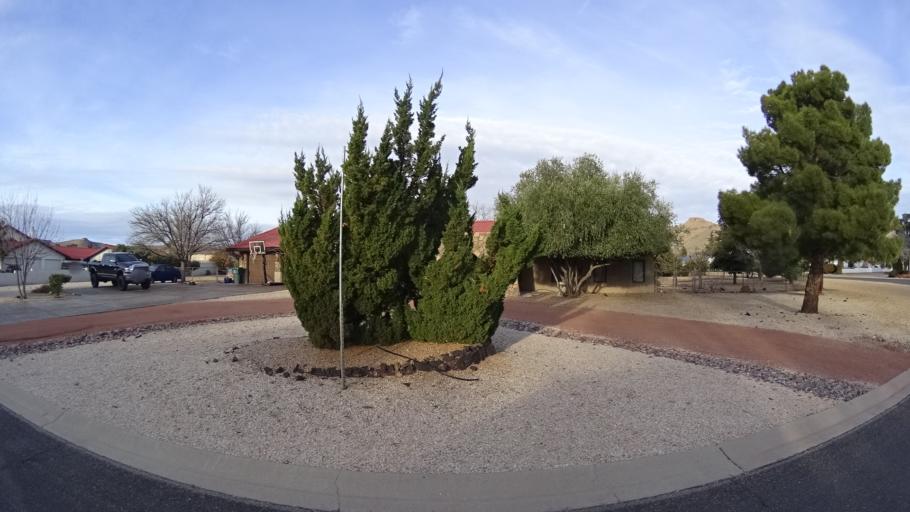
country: US
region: Arizona
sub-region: Mohave County
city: New Kingman-Butler
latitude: 35.2429
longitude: -114.0439
